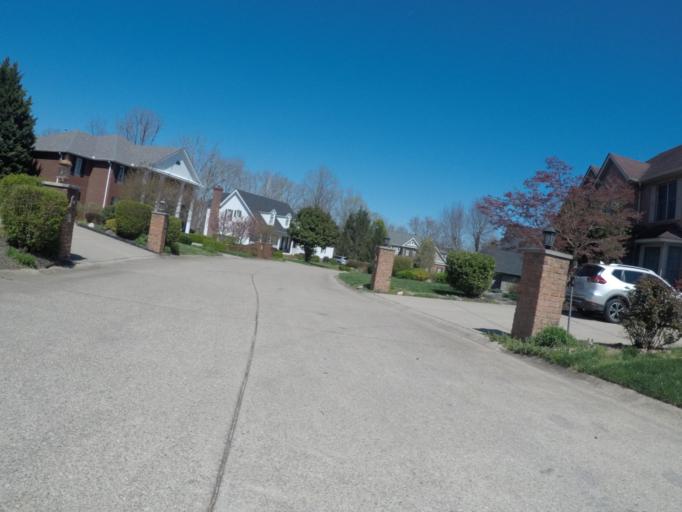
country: US
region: West Virginia
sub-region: Cabell County
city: Pea Ridge
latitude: 38.4196
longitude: -82.3143
